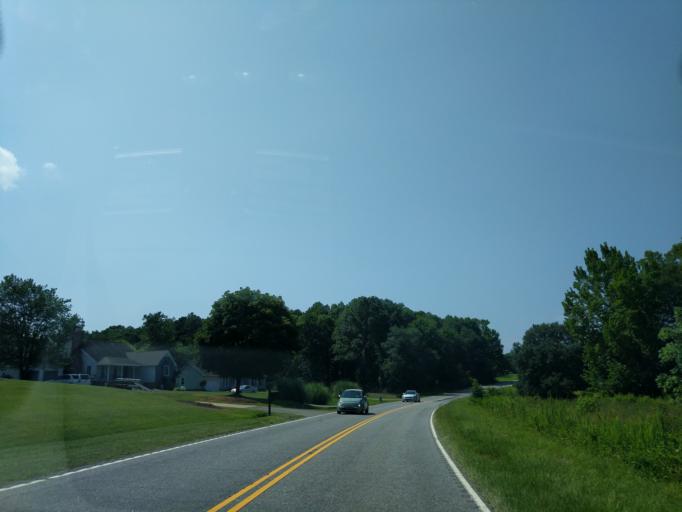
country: US
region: South Carolina
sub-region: Greenville County
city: Greer
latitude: 34.9653
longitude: -82.1924
